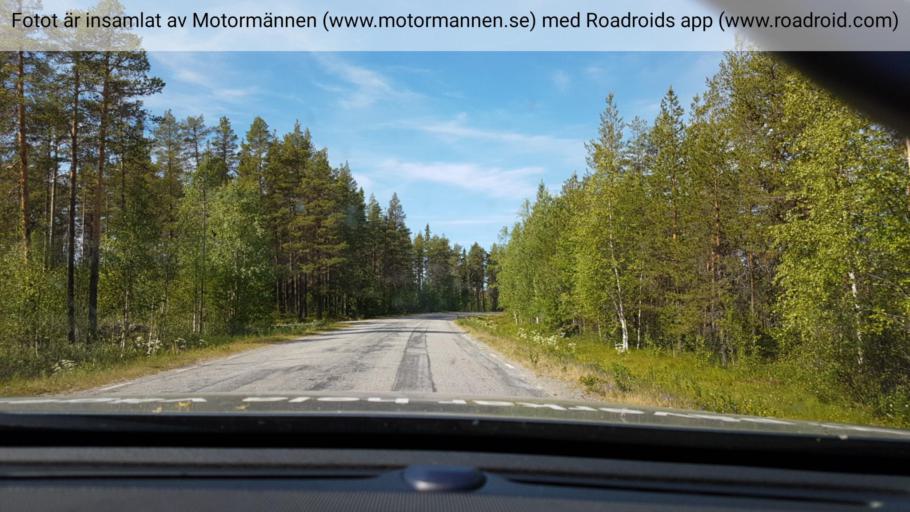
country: SE
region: Vaesterbotten
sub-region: Dorotea Kommun
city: Dorotea
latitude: 64.3674
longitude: 16.1637
